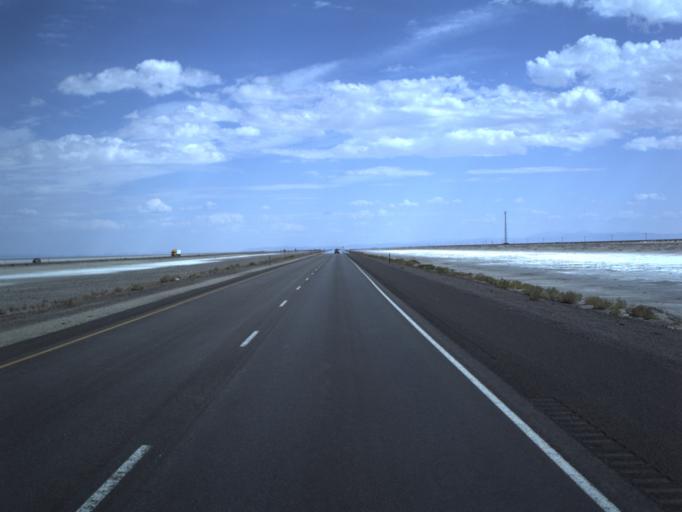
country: US
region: Utah
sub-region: Tooele County
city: Wendover
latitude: 40.7377
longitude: -113.8133
